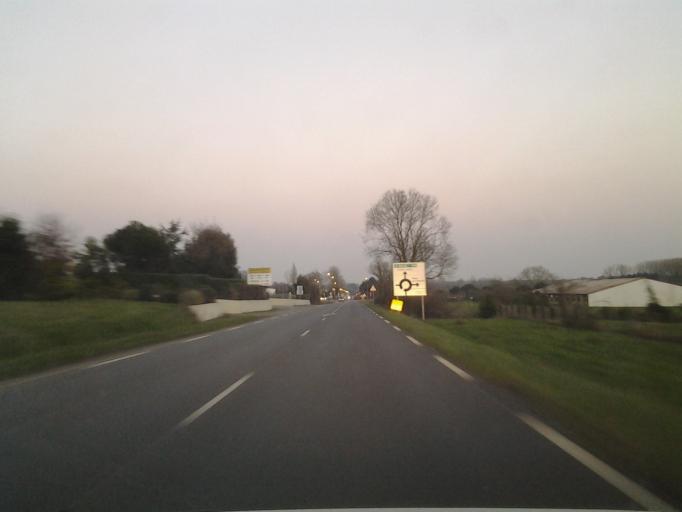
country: FR
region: Pays de la Loire
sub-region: Departement de la Vendee
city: Saint-Gervais
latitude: 46.9046
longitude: -2.0177
